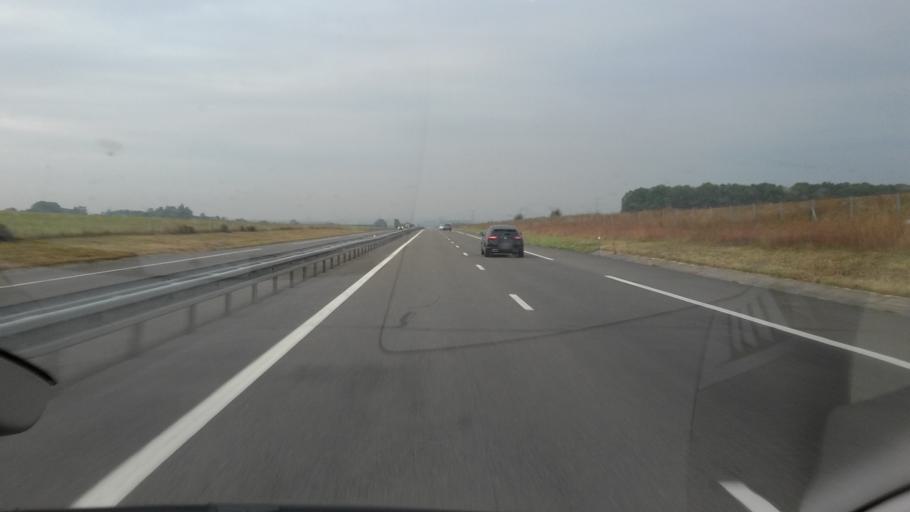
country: FR
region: Champagne-Ardenne
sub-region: Departement des Ardennes
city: Attigny
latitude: 49.5846
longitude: 4.4883
